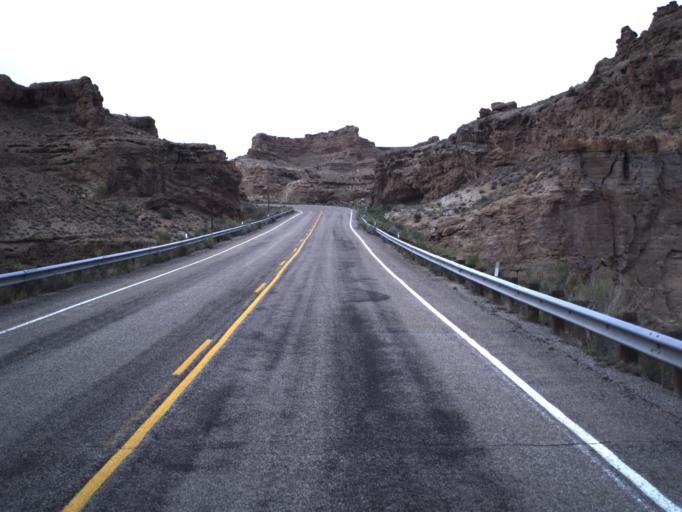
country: US
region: Colorado
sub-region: Rio Blanco County
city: Rangely
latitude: 39.9808
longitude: -109.1775
